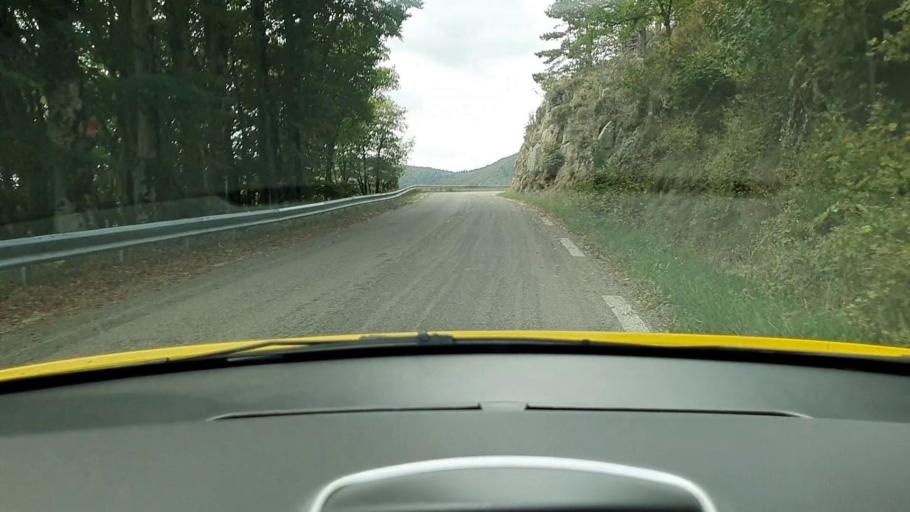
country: FR
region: Languedoc-Roussillon
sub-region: Departement du Gard
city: Le Vigan
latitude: 44.0409
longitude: 3.5634
